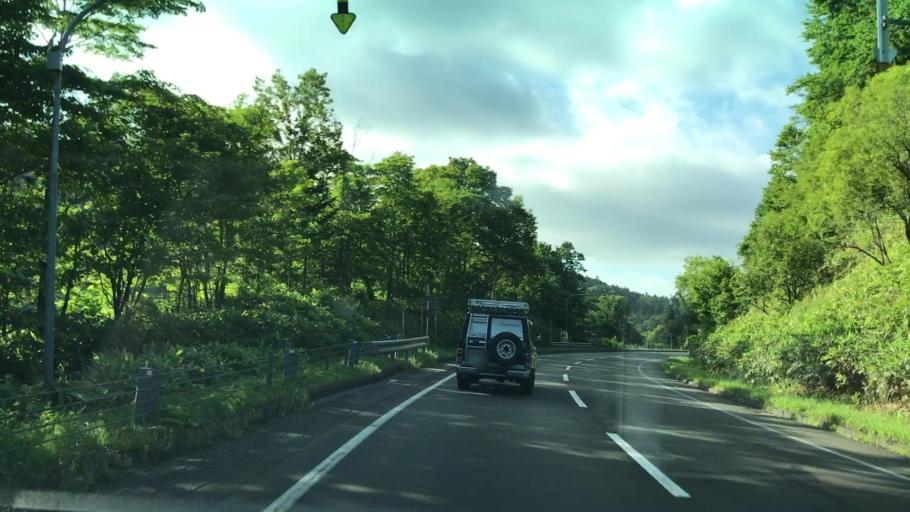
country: JP
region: Hokkaido
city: Iwamizawa
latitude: 42.9103
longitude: 142.1220
